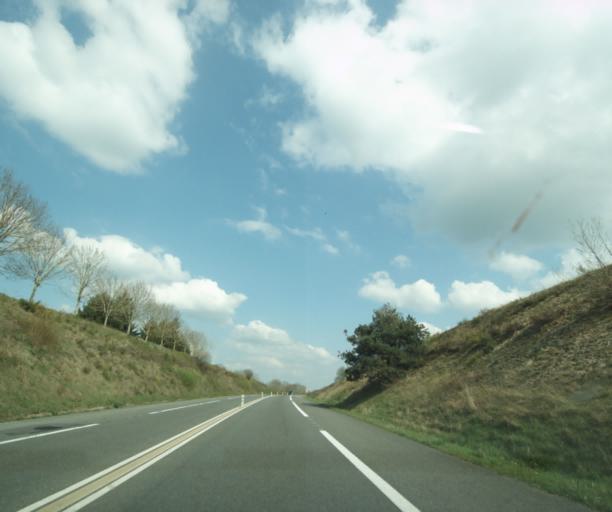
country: FR
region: Auvergne
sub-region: Departement de l'Allier
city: Buxieres-les-Mines
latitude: 46.3996
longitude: 3.0466
